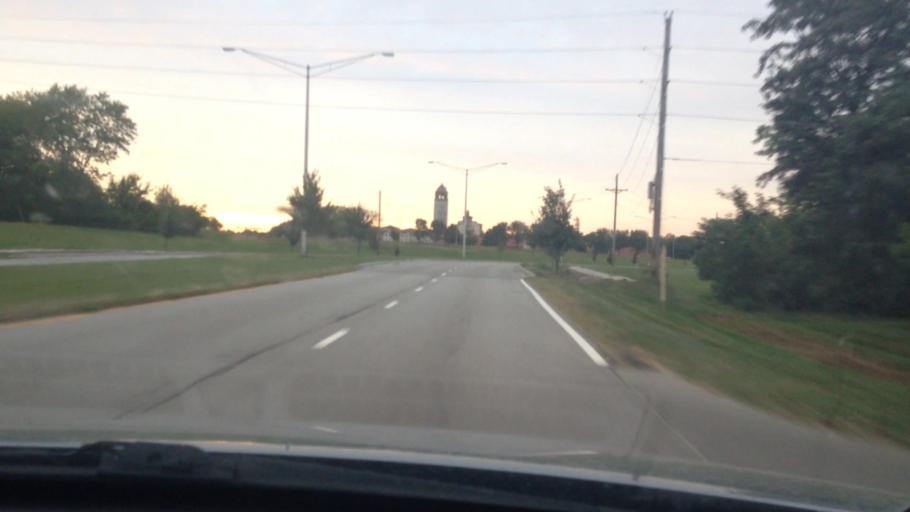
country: US
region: Missouri
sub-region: Jackson County
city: Lees Summit
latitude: 38.9401
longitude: -94.4047
